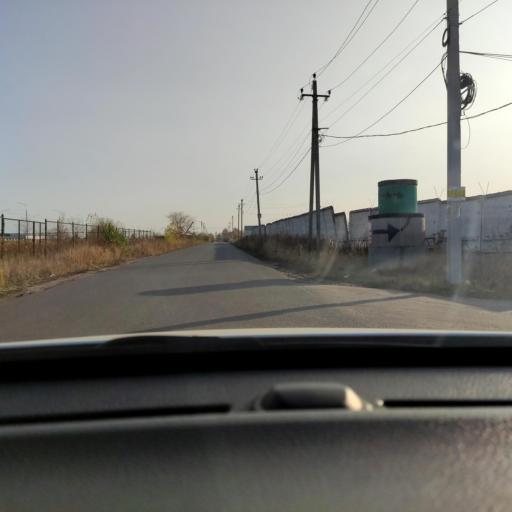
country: RU
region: Voronezj
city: Somovo
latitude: 51.6770
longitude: 39.3107
